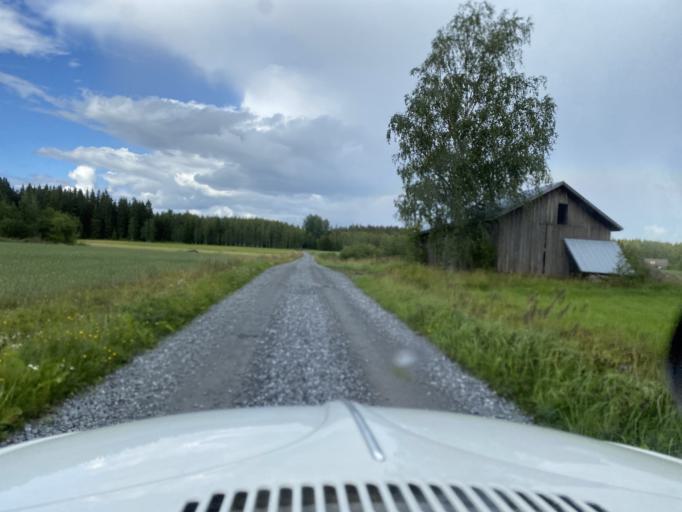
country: FI
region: Pirkanmaa
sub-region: Lounais-Pirkanmaa
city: Punkalaidun
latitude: 61.1321
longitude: 23.0665
